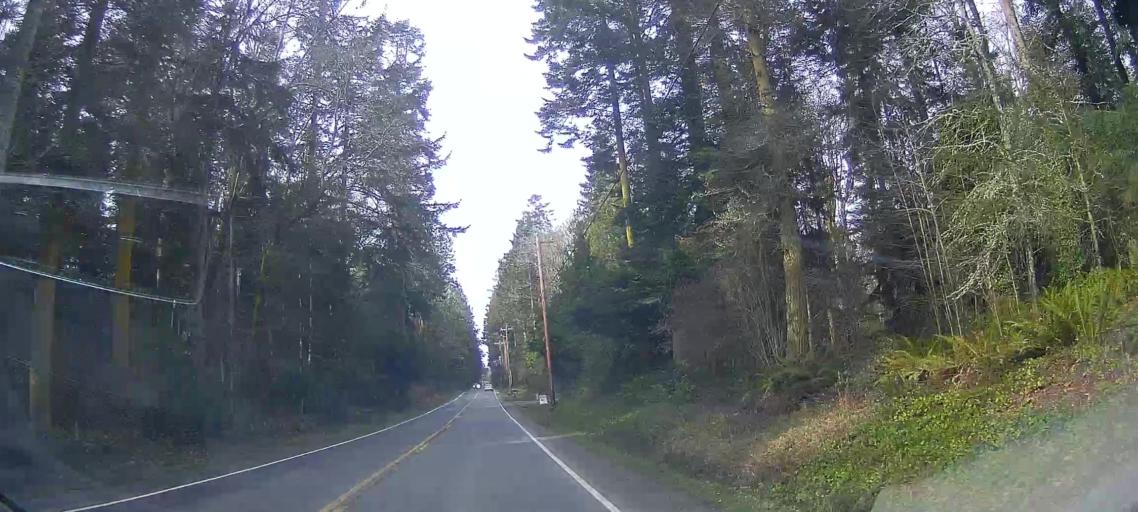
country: US
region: Washington
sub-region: Island County
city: Camano
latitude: 48.1234
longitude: -122.4540
